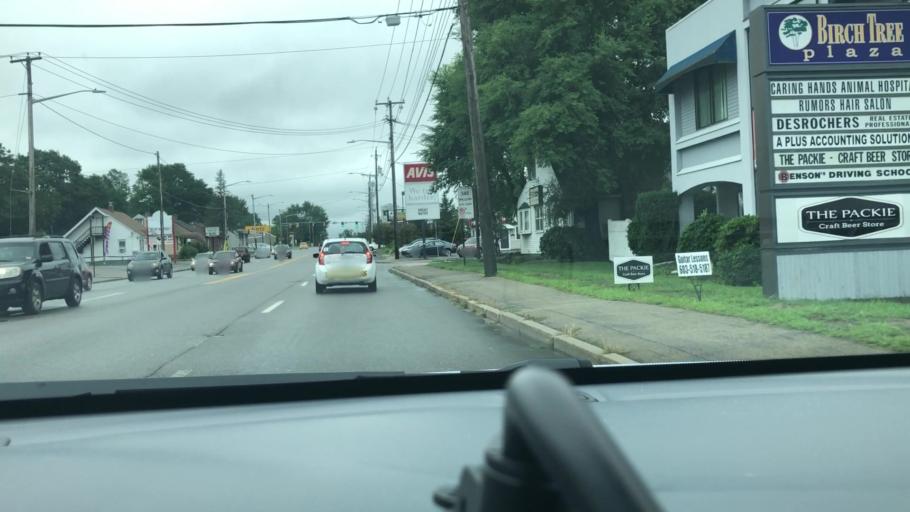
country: US
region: New Hampshire
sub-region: Hillsborough County
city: Manchester
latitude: 42.9692
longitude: -71.4530
